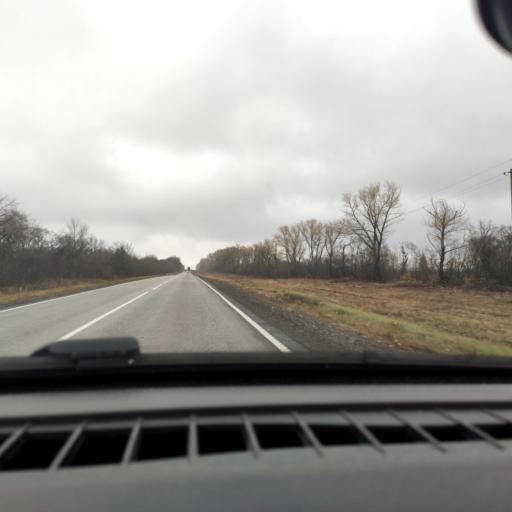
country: RU
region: Voronezj
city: Uryv-Pokrovka
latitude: 51.0785
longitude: 38.9973
